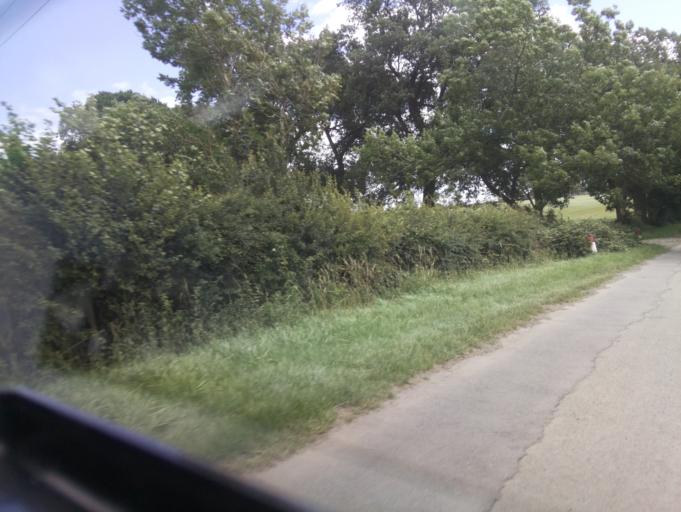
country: GB
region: England
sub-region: Nottinghamshire
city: Cotgrave
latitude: 52.8590
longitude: -1.0532
